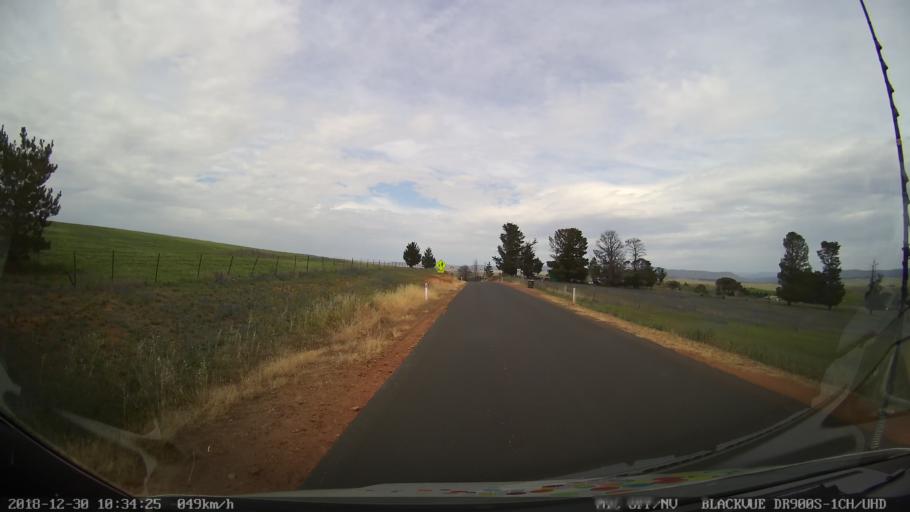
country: AU
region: New South Wales
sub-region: Snowy River
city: Berridale
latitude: -36.5008
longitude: 148.8408
